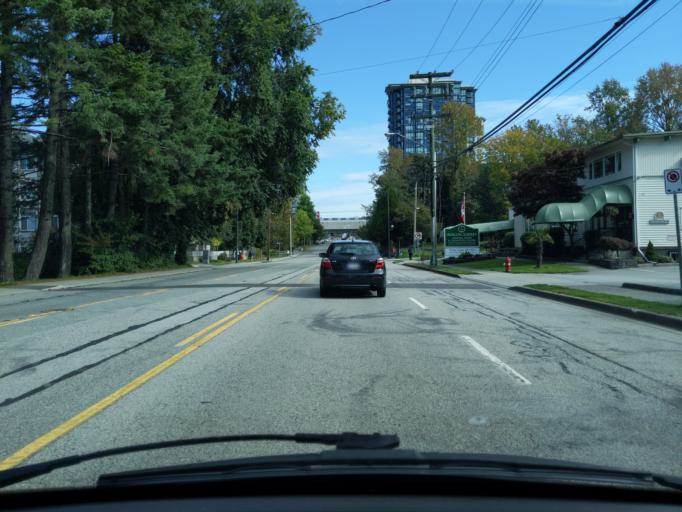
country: CA
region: British Columbia
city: New Westminster
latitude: 49.1989
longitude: -122.8549
